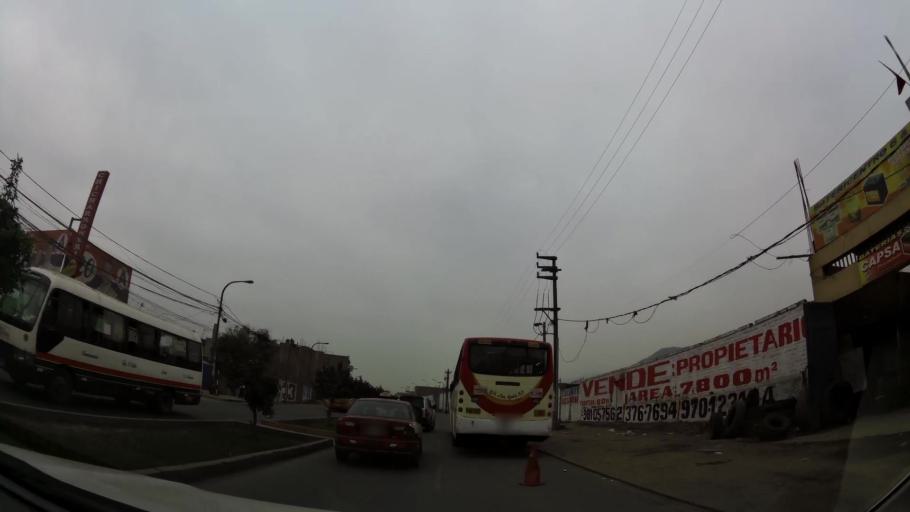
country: PE
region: Lima
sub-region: Lima
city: Independencia
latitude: -11.9819
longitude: -76.9926
